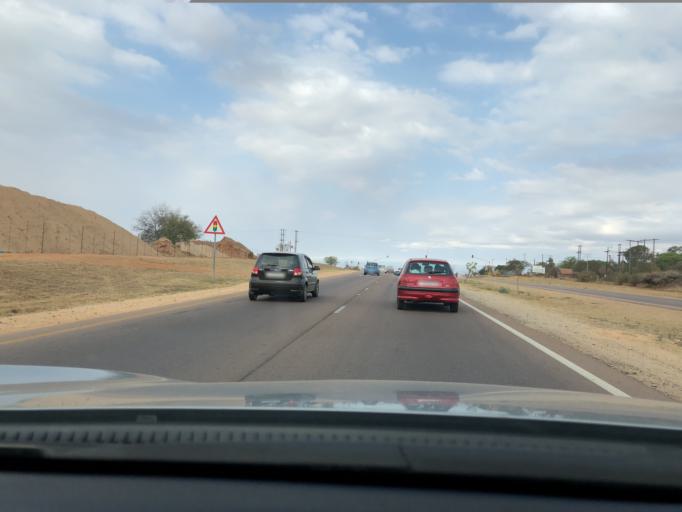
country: ZA
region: Limpopo
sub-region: Capricorn District Municipality
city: Polokwane
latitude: -23.8985
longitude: 29.5145
